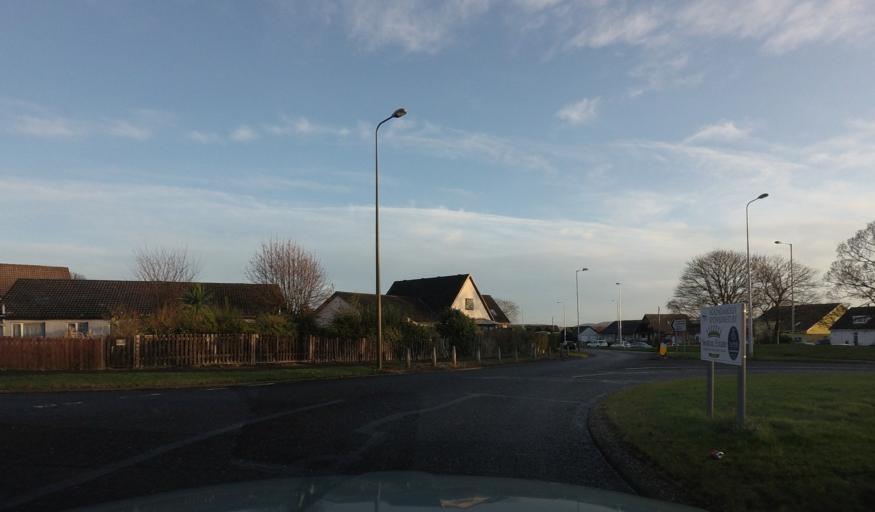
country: GB
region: Scotland
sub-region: Angus
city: Muirhead
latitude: 56.4589
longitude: -3.0393
